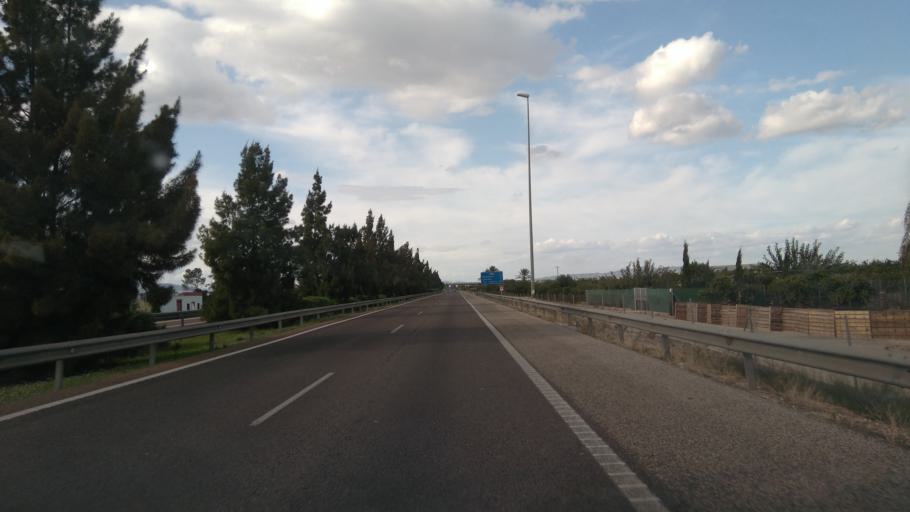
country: ES
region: Valencia
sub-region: Provincia de Valencia
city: Guadassuar
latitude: 39.1651
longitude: -0.4588
